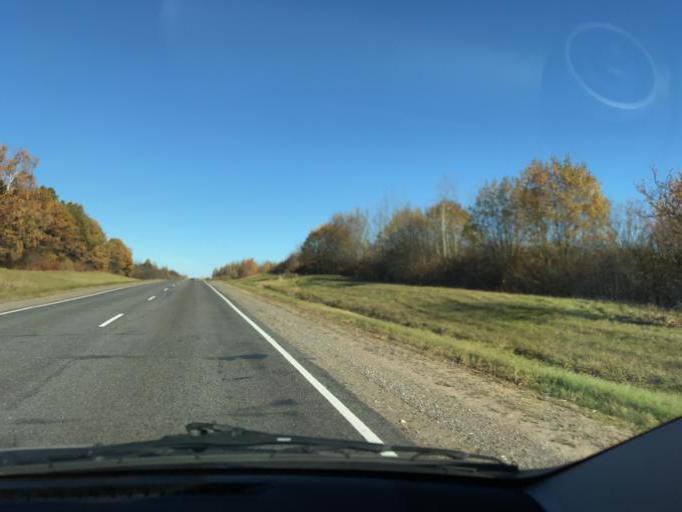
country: BY
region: Vitebsk
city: Lyepyel'
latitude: 55.0192
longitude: 28.7426
